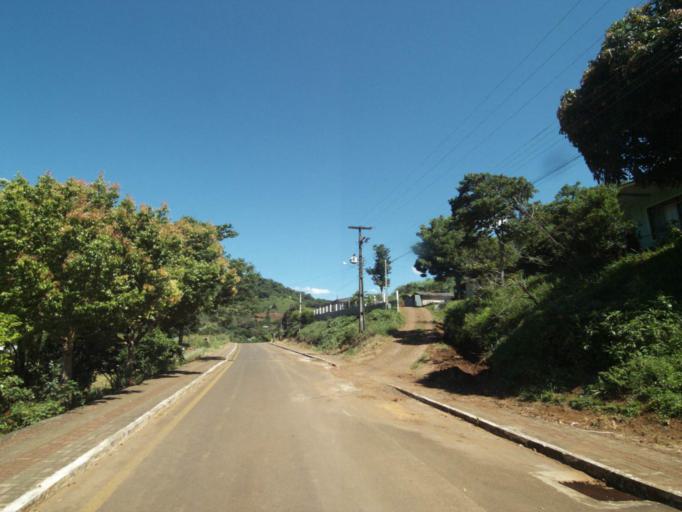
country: BR
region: Parana
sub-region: Ampere
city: Ampere
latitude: -26.1759
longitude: -53.3574
